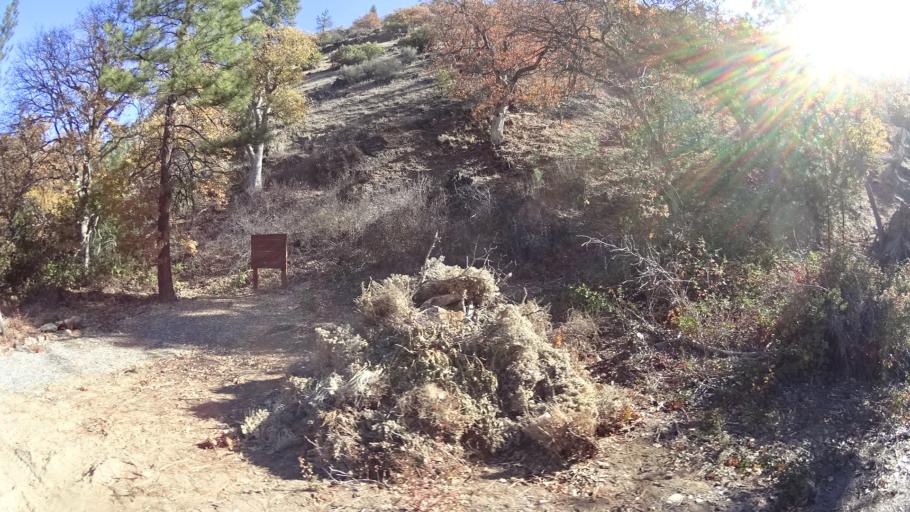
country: US
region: California
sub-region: Siskiyou County
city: Yreka
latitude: 41.8654
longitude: -122.8177
